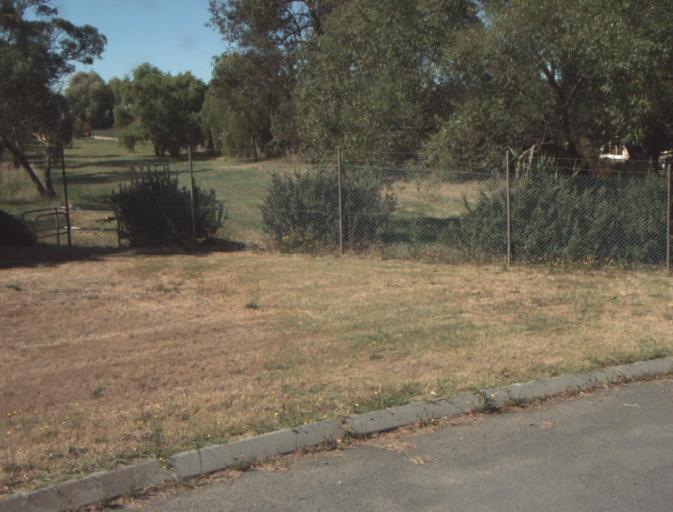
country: AU
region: Tasmania
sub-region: Launceston
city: Newnham
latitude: -41.4134
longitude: 147.1381
